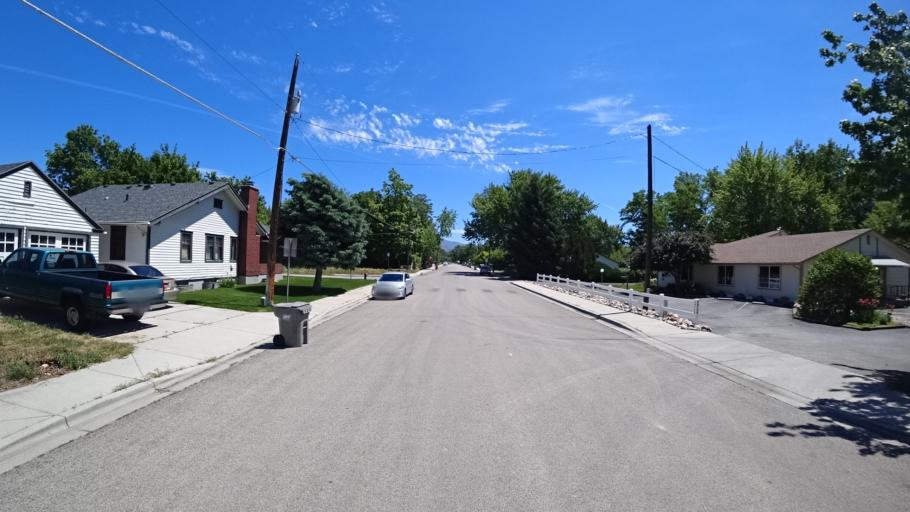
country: US
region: Idaho
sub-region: Ada County
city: Garden City
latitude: 43.5988
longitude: -116.2391
